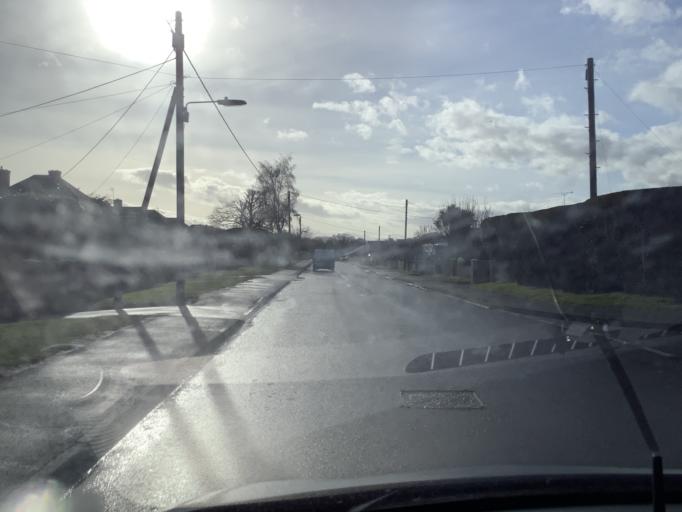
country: GB
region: England
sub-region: Hampshire
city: Hythe
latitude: 50.8315
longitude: -1.3862
